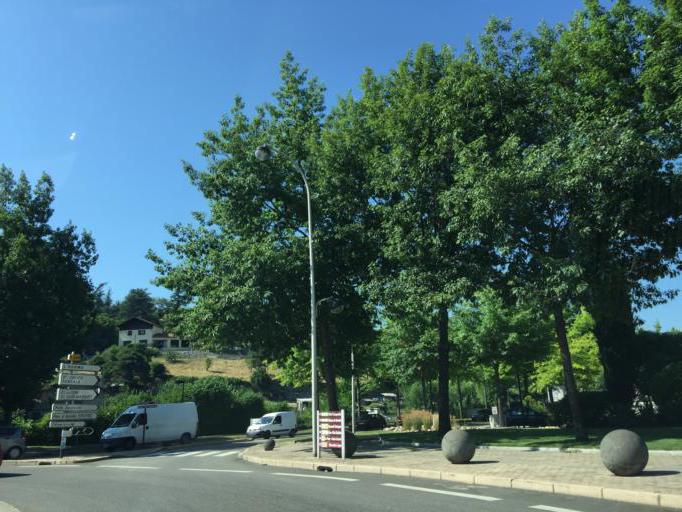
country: FR
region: Rhone-Alpes
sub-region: Departement de la Loire
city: Saint-Chamond
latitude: 45.4716
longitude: 4.5026
